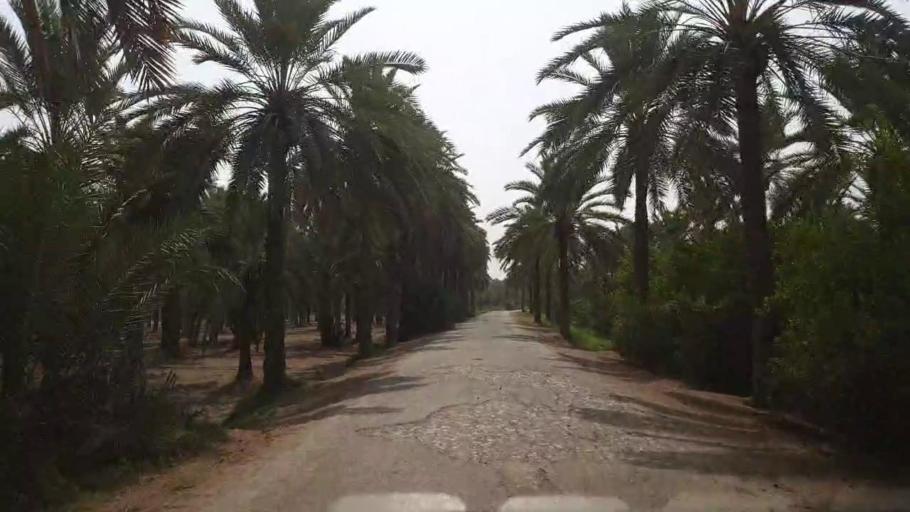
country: PK
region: Sindh
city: Gambat
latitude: 27.4074
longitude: 68.5542
